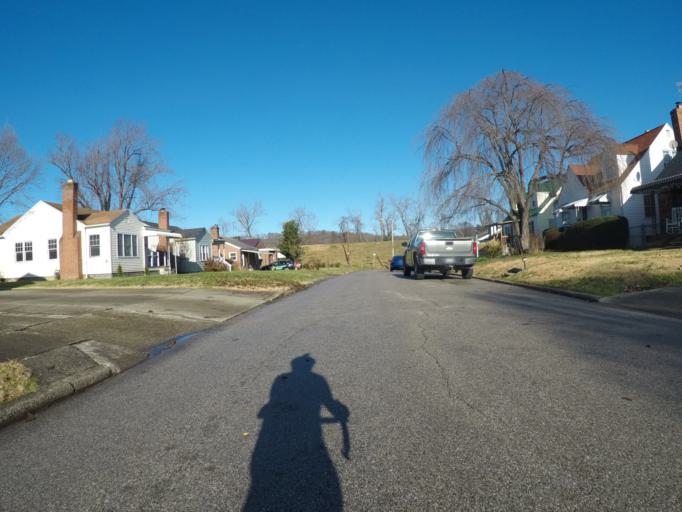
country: US
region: Ohio
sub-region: Lawrence County
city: Burlington
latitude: 38.4050
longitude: -82.5084
